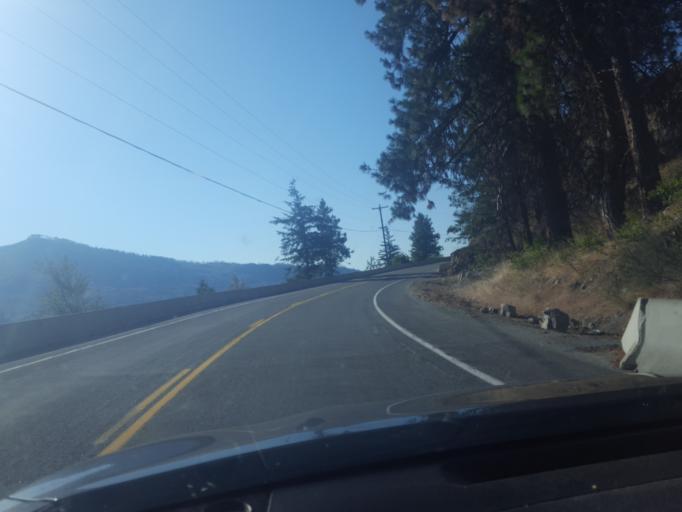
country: US
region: Washington
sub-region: Chelan County
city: Granite Falls
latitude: 47.9795
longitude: -120.2230
